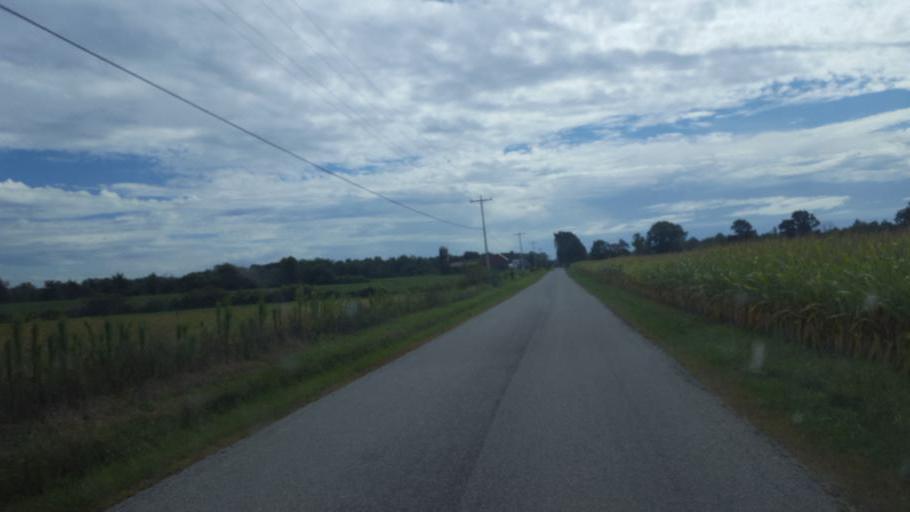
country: US
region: Ohio
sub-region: Licking County
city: Johnstown
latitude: 40.1084
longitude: -82.7232
